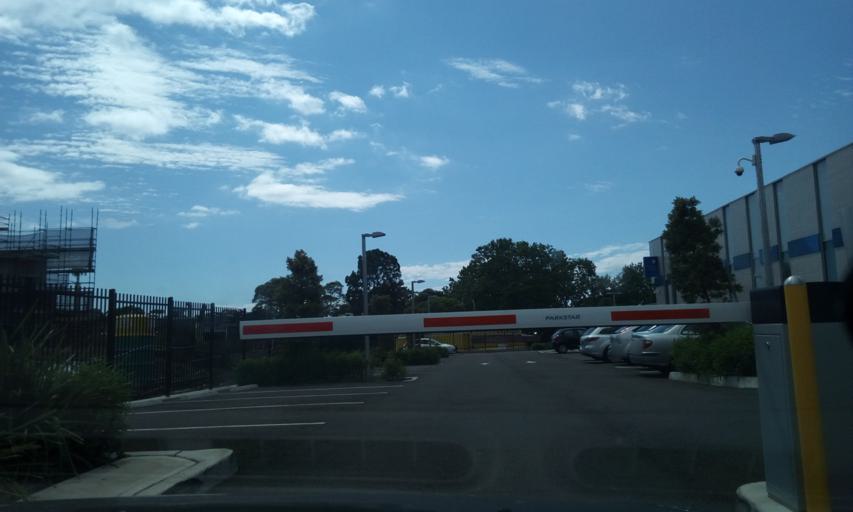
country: AU
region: New South Wales
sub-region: Wollongong
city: Corrimal
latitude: -34.3719
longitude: 150.8957
